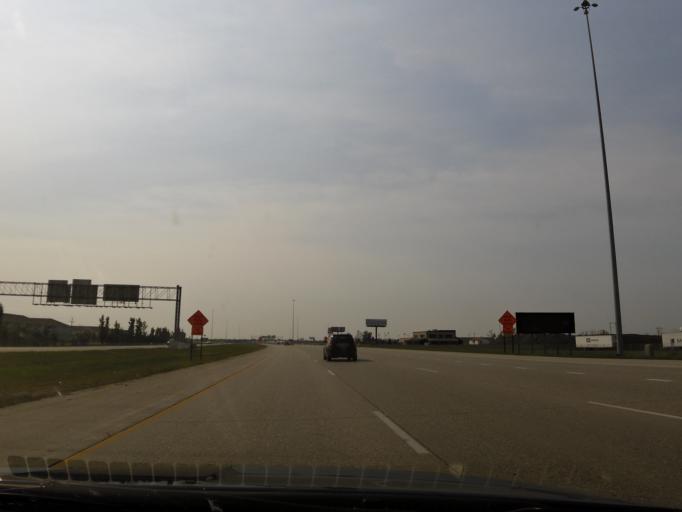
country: US
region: North Dakota
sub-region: Cass County
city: Fargo
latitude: 46.8417
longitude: -96.8411
